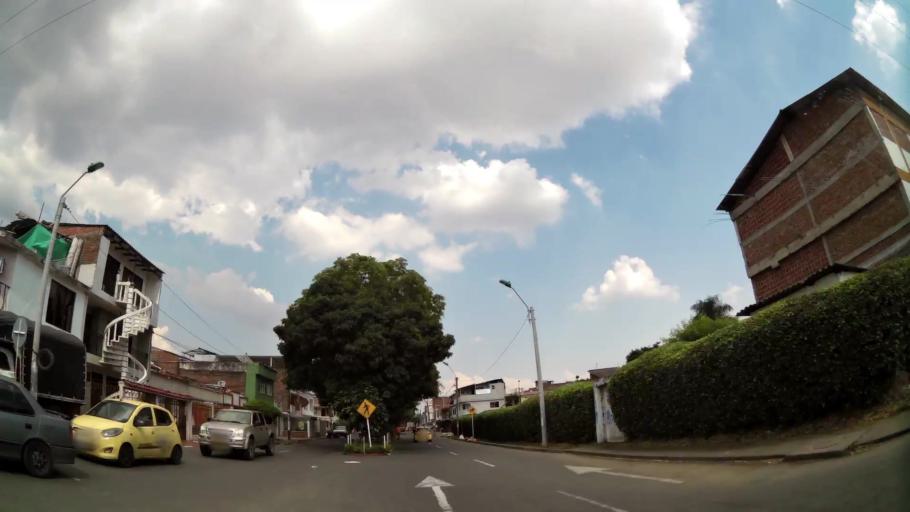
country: CO
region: Valle del Cauca
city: Cali
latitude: 3.4163
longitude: -76.5212
